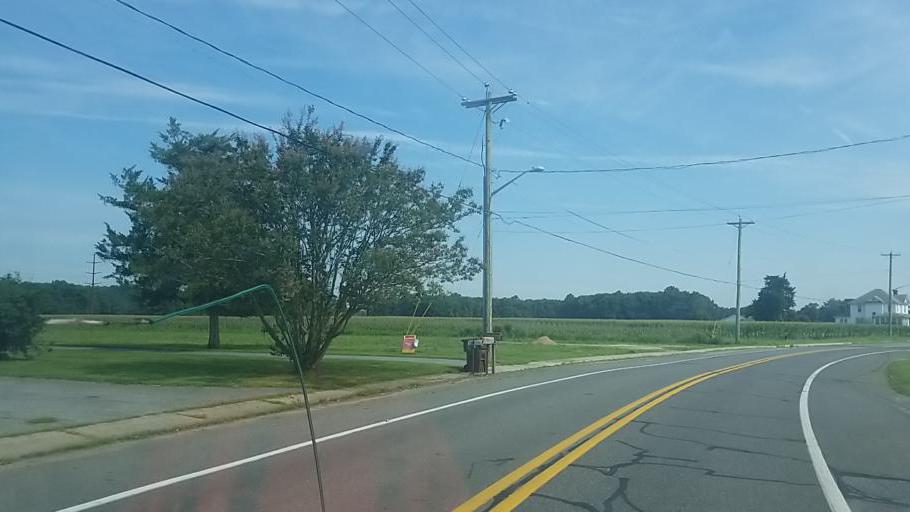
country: US
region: Delaware
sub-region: Sussex County
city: Selbyville
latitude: 38.5253
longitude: -75.2382
